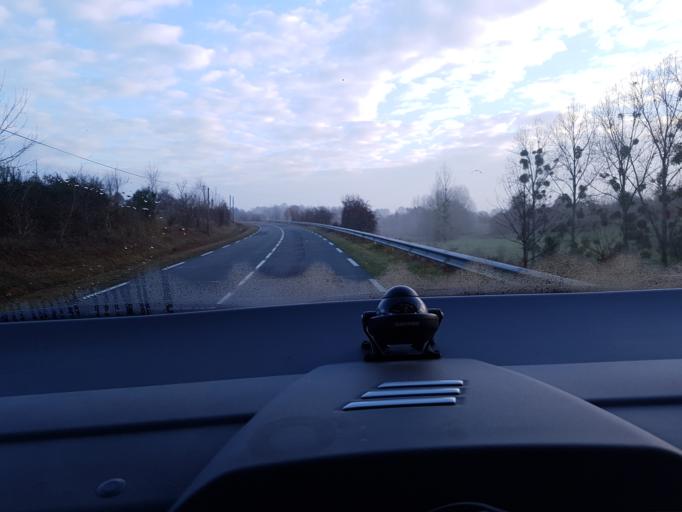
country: FR
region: Lower Normandy
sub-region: Departement de l'Orne
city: Champsecret
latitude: 48.6169
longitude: -0.5831
